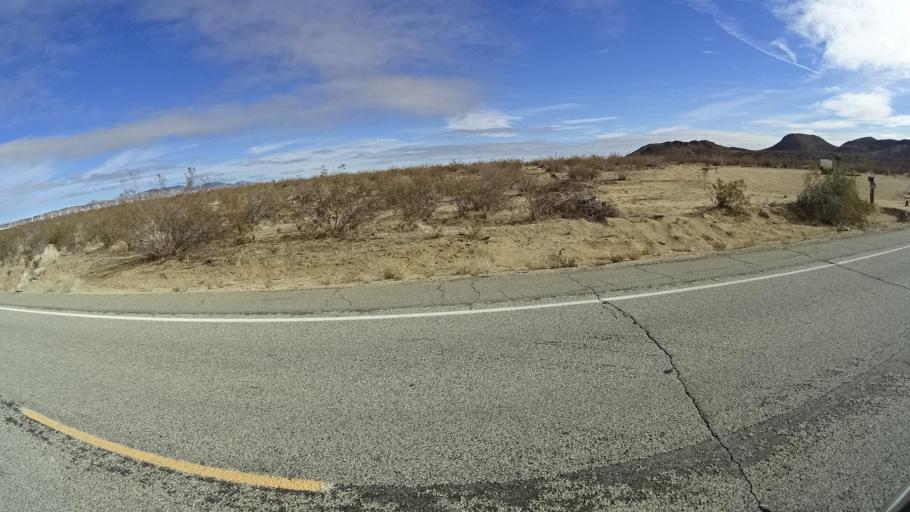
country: US
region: California
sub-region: Kern County
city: Mojave
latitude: 34.9706
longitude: -118.3041
